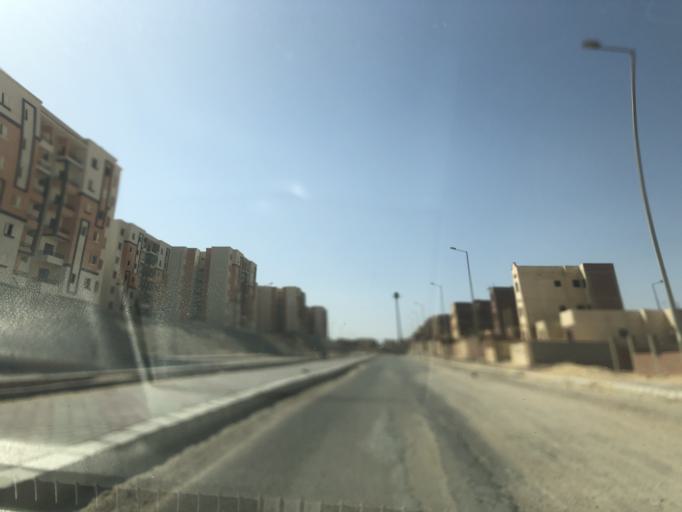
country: EG
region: Al Jizah
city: Madinat Sittah Uktubar
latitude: 29.9341
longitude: 30.9813
